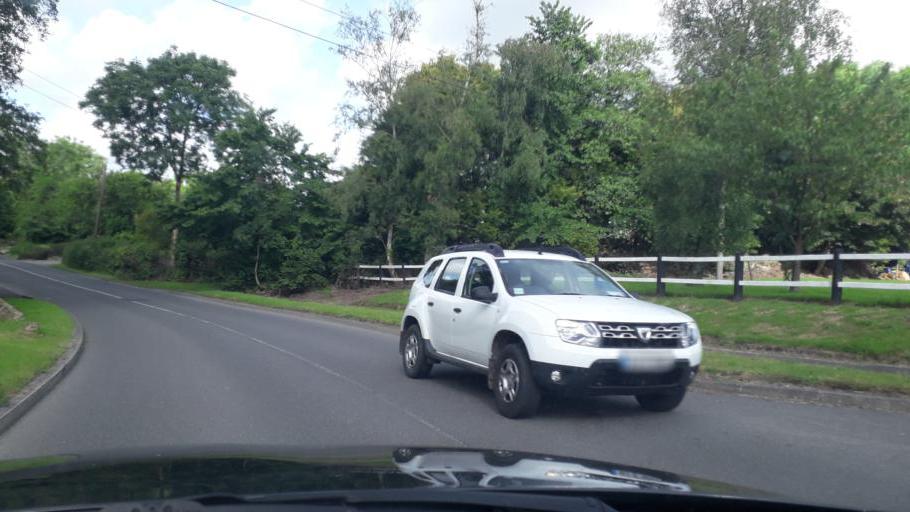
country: IE
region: Leinster
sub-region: Loch Garman
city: Loch Garman
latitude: 52.2865
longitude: -6.5274
